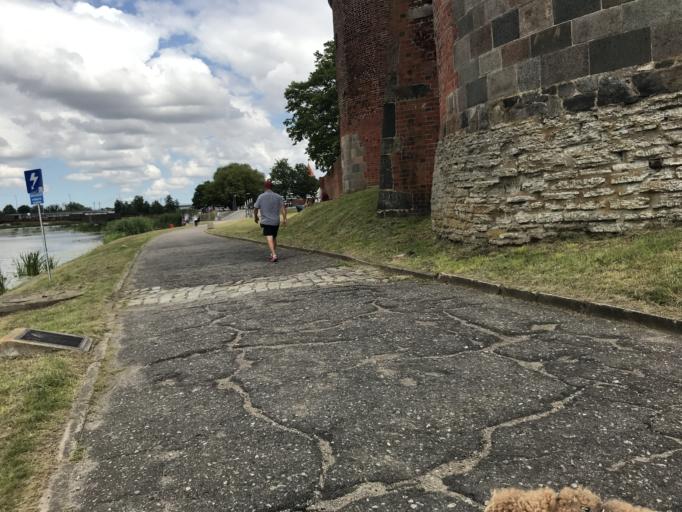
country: PL
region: Pomeranian Voivodeship
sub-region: Powiat malborski
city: Malbork
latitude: 54.0401
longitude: 19.0262
